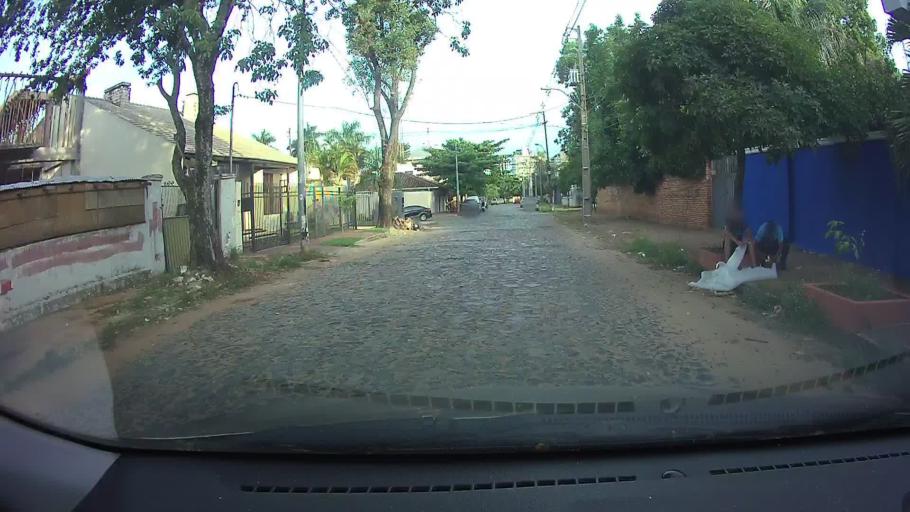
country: PY
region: Asuncion
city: Asuncion
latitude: -25.2775
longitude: -57.5730
